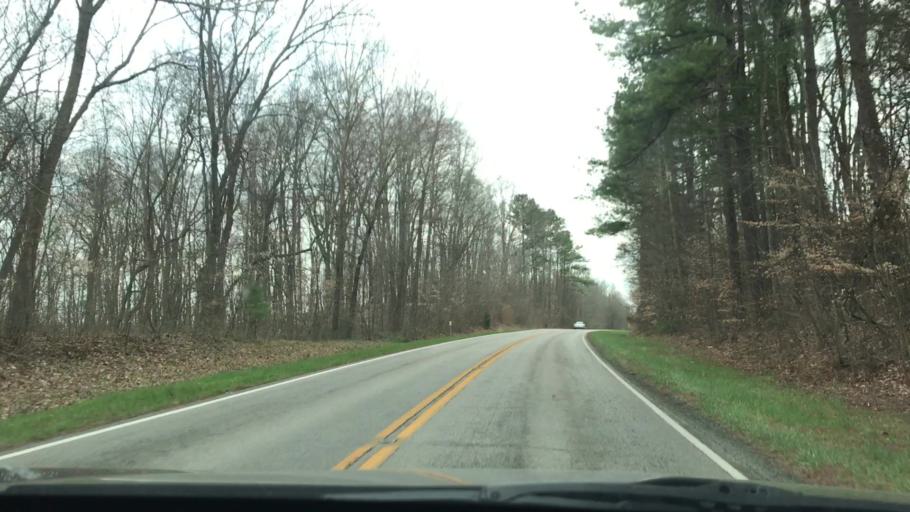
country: US
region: Kentucky
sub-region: Hart County
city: Munfordville
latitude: 37.3110
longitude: -85.7621
